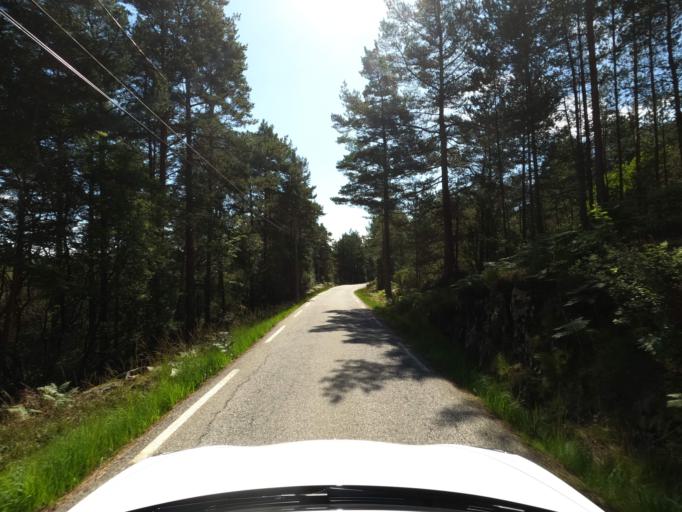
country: NO
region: Hordaland
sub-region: Os
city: Hagavik
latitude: 60.1660
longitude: 5.3664
